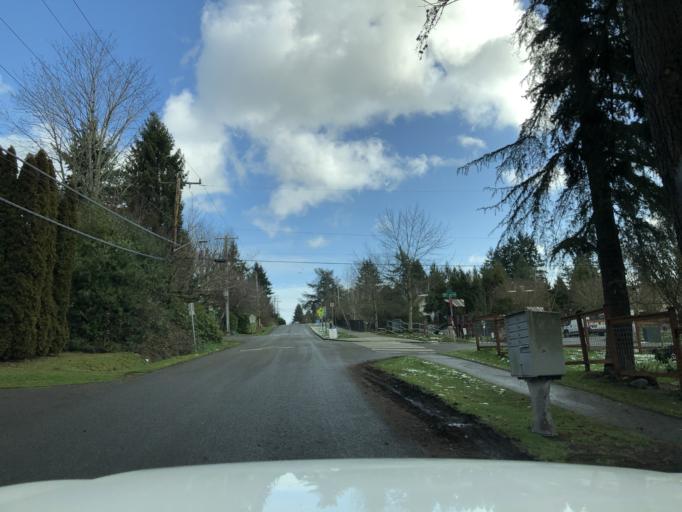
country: US
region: Washington
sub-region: King County
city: Lake Forest Park
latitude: 47.7264
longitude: -122.2891
